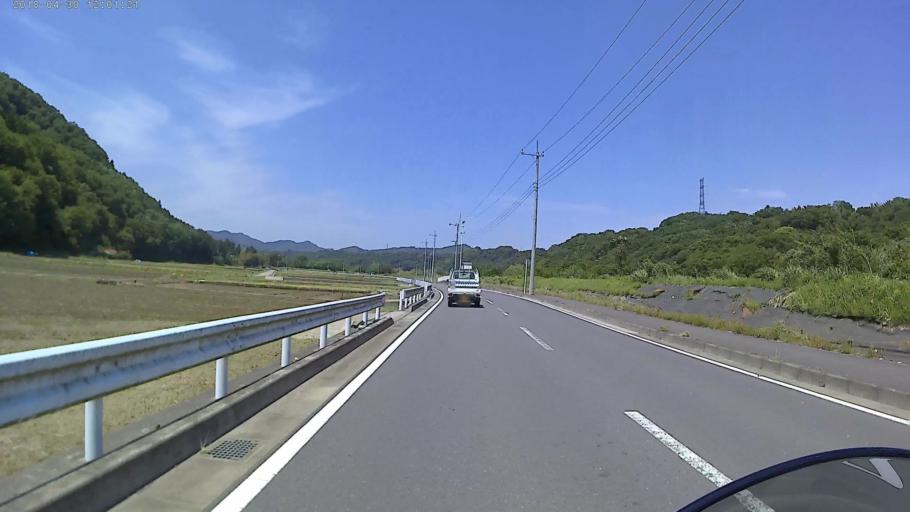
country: JP
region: Kanagawa
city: Zama
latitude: 35.5166
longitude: 139.3259
